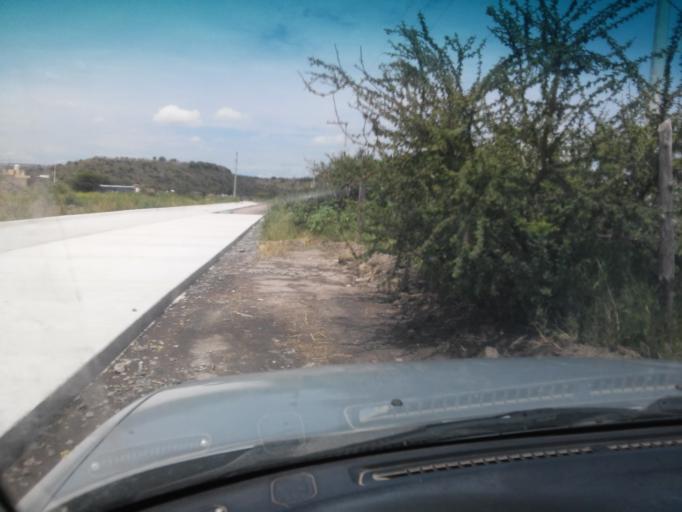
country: MX
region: Durango
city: Victoria de Durango
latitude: 23.9980
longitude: -104.7057
